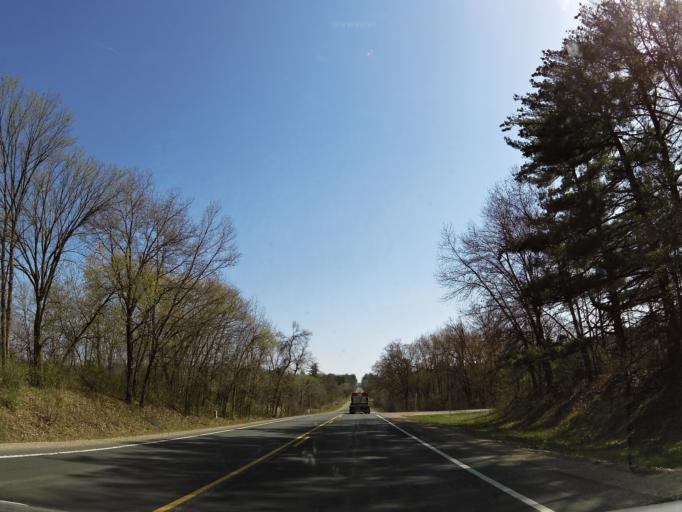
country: US
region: Wisconsin
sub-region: Pepin County
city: Durand
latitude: 44.7389
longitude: -91.9331
